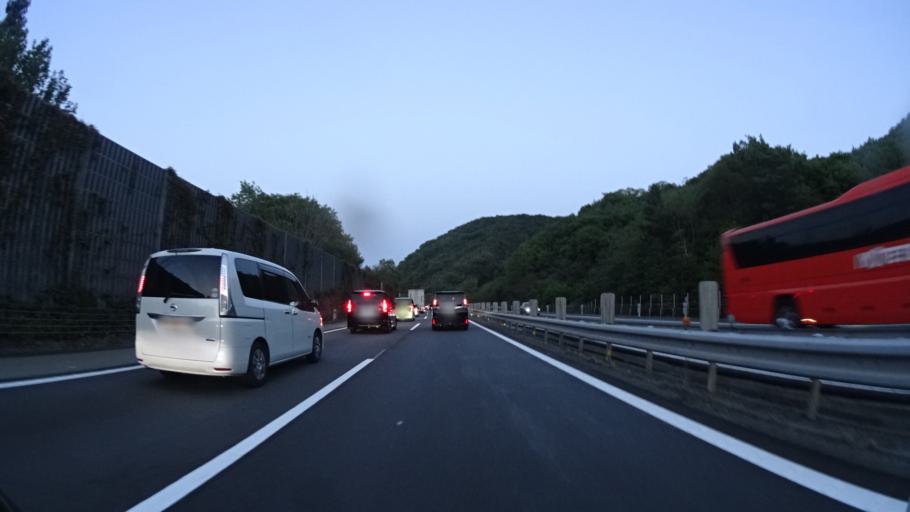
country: JP
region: Hyogo
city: Kariya
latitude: 34.7823
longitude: 134.2858
